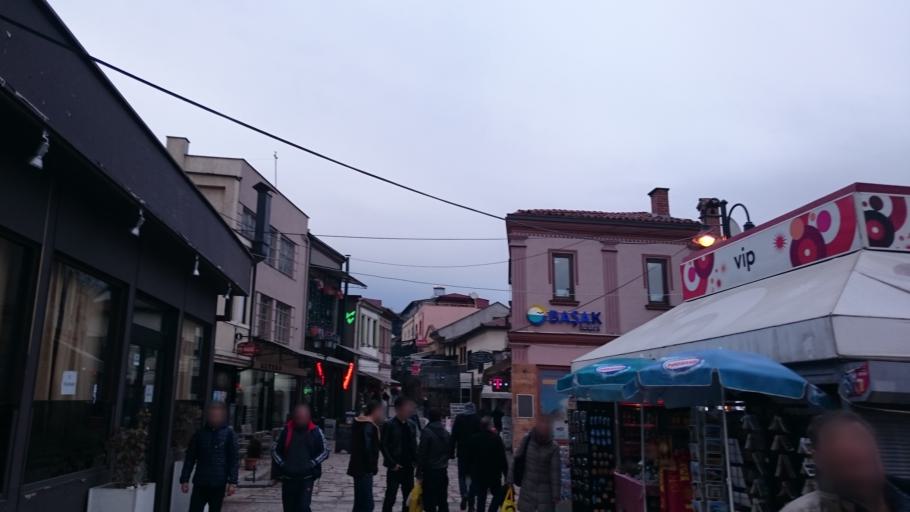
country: MK
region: Karpos
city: Skopje
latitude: 41.9992
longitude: 21.4356
